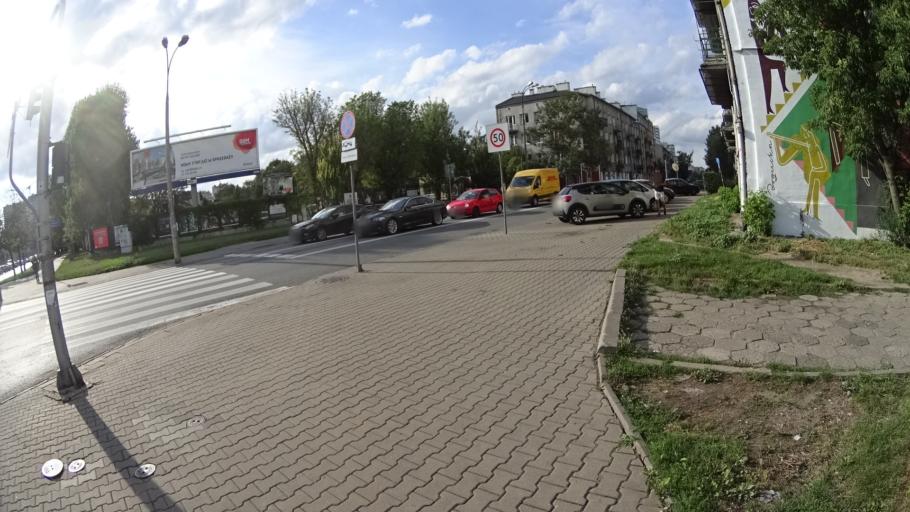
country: PL
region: Masovian Voivodeship
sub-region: Warszawa
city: Ochota
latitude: 52.2289
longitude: 20.9676
